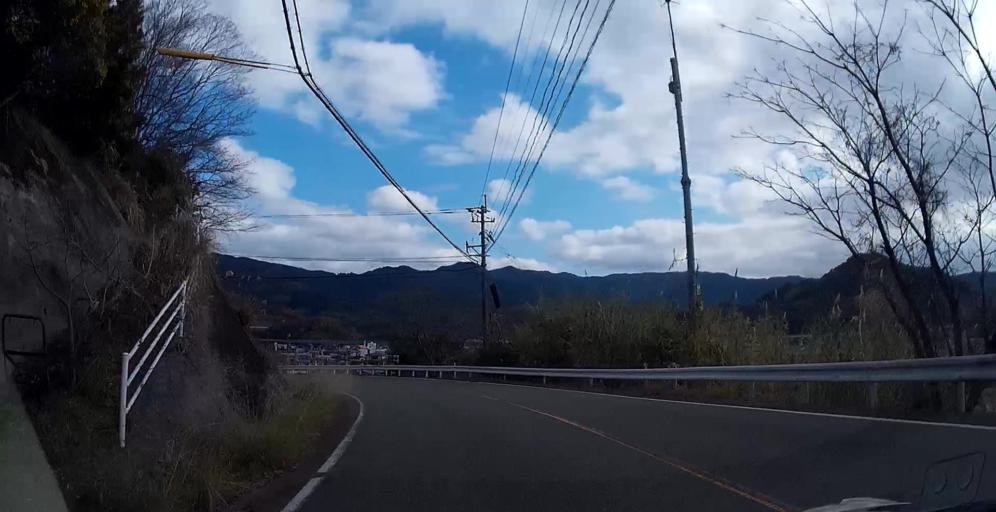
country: JP
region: Kumamoto
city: Yatsushiro
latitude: 32.3654
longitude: 130.5070
